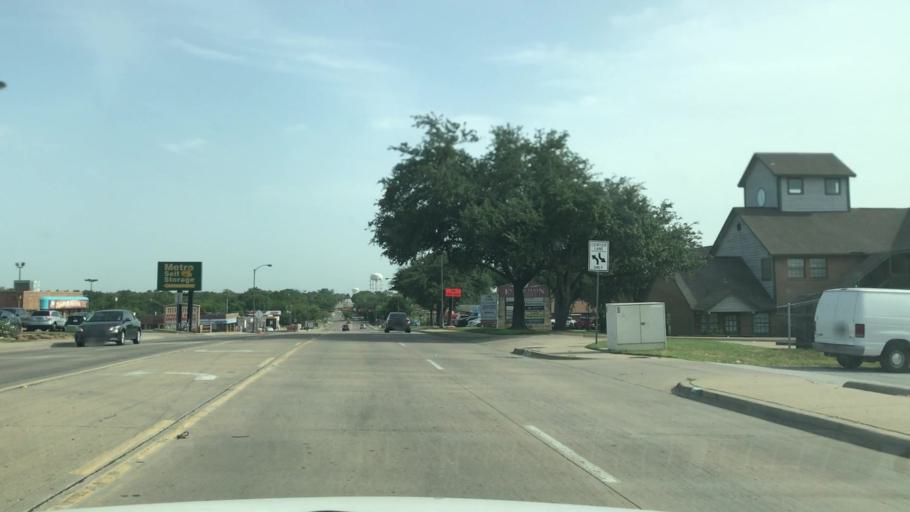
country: US
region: Texas
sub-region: Tarrant County
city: Euless
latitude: 32.8417
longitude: -97.0826
